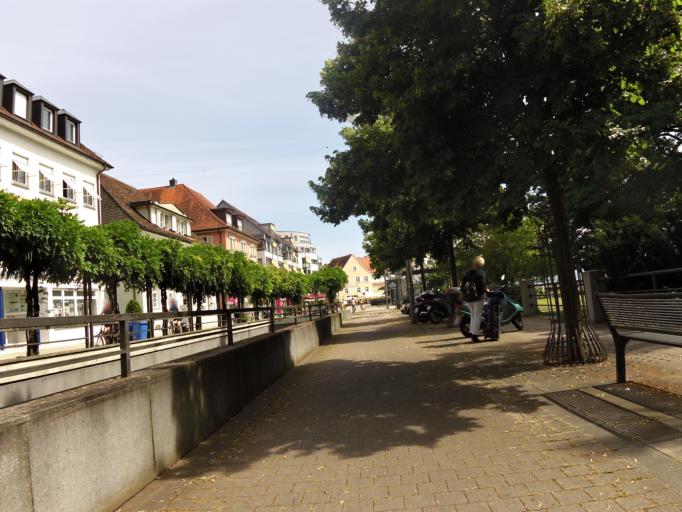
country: DE
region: Baden-Wuerttemberg
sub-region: Tuebingen Region
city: Friedrichshafen
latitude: 47.6509
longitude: 9.4777
